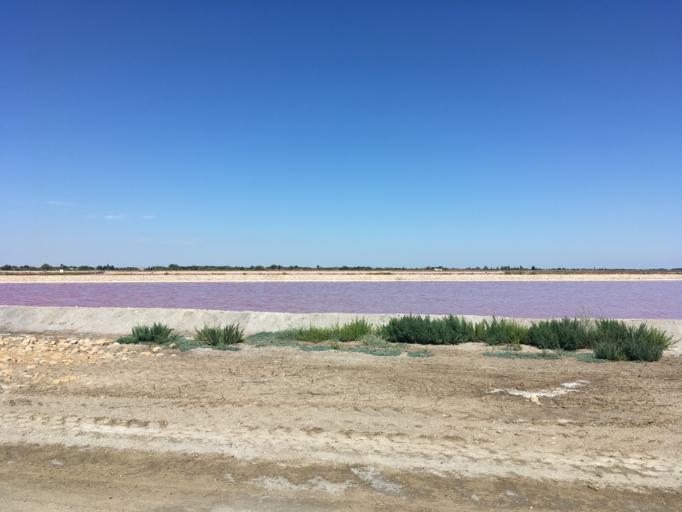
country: FR
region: Languedoc-Roussillon
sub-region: Departement du Gard
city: Aigues-Mortes
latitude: 43.5478
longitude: 4.1872
